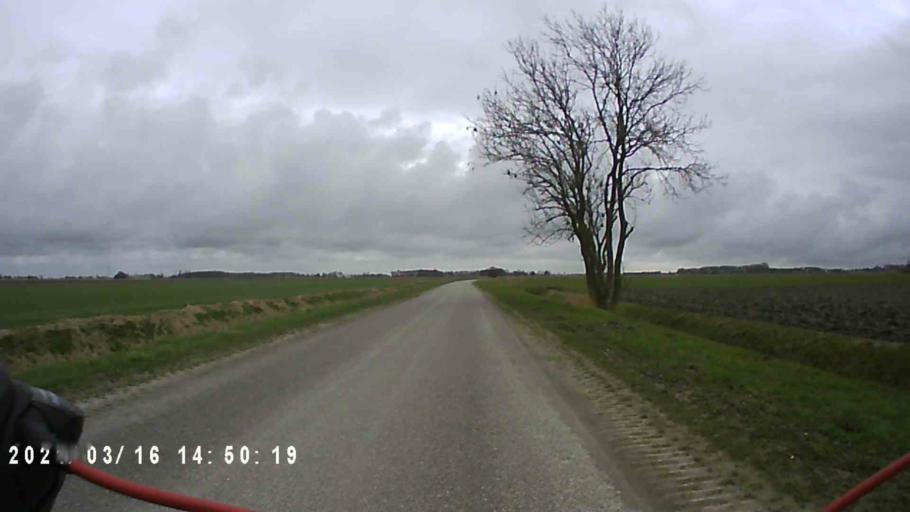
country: NL
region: Friesland
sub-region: Gemeente Harlingen
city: Harlingen
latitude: 53.1197
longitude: 5.4624
